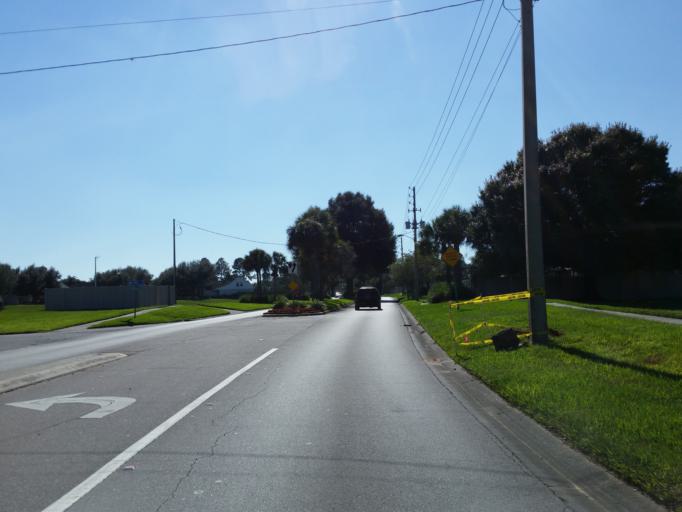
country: US
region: Florida
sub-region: Hillsborough County
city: Brandon
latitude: 27.9334
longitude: -82.2613
